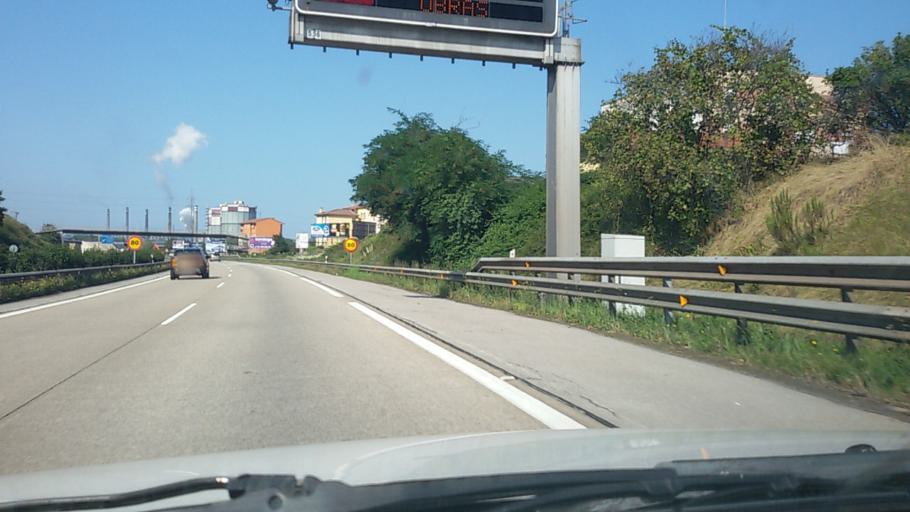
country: ES
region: Asturias
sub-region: Province of Asturias
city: Aviles
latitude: 43.5528
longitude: -5.8844
